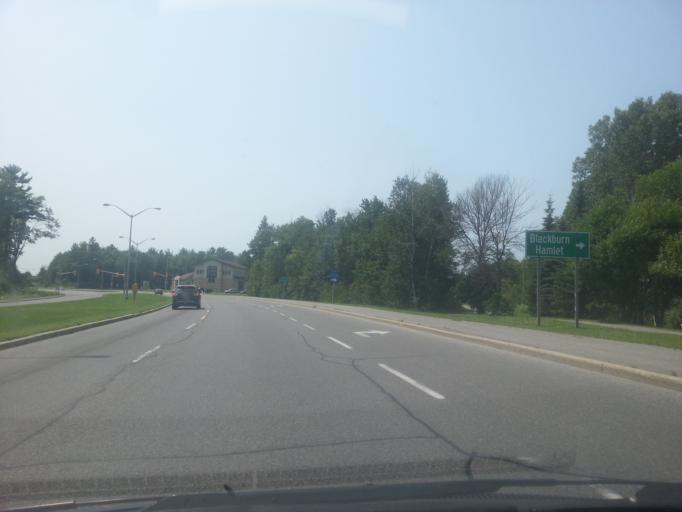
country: CA
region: Ontario
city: Ottawa
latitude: 45.4414
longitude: -75.5401
